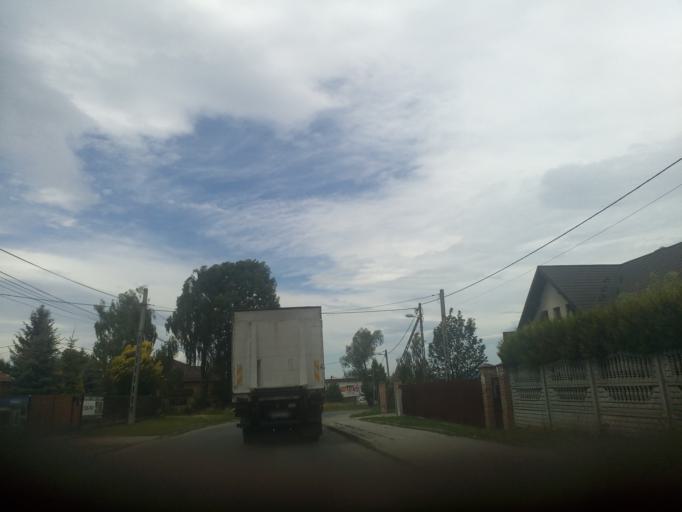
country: PL
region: Lesser Poland Voivodeship
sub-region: Powiat nowosadecki
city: Nowy Sacz
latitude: 49.5914
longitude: 20.7093
